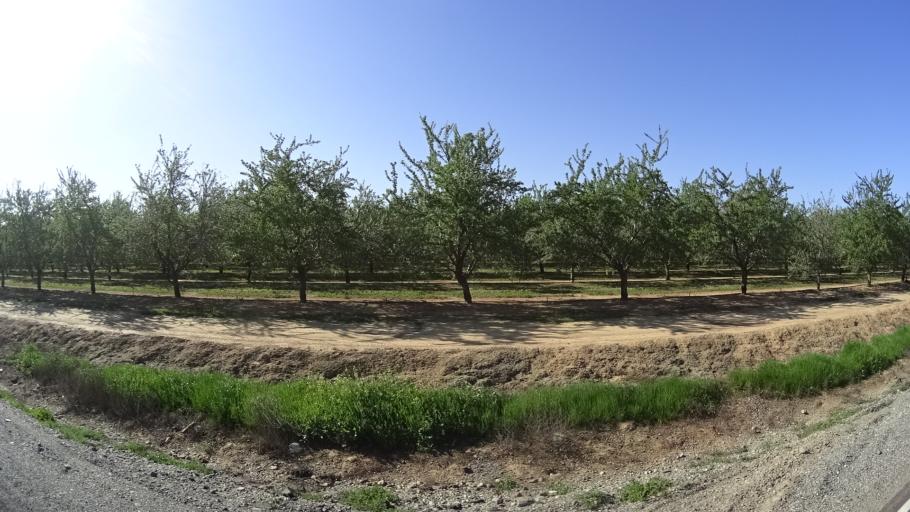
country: US
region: California
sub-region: Glenn County
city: Hamilton City
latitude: 39.7665
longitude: -122.0851
